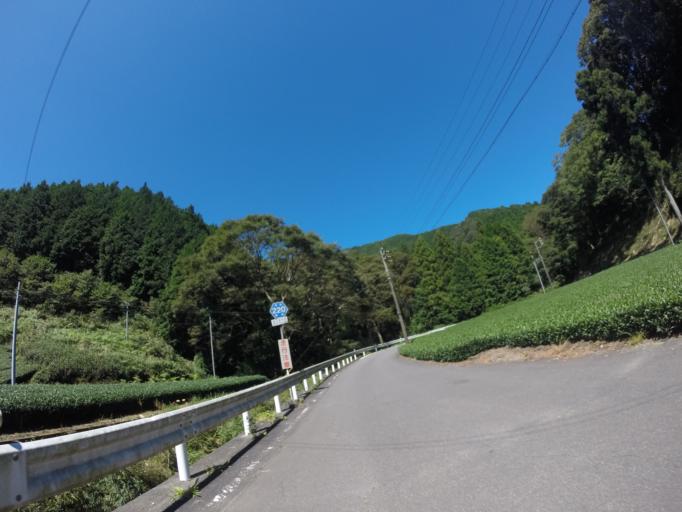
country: JP
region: Shizuoka
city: Fujieda
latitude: 34.9679
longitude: 138.1916
